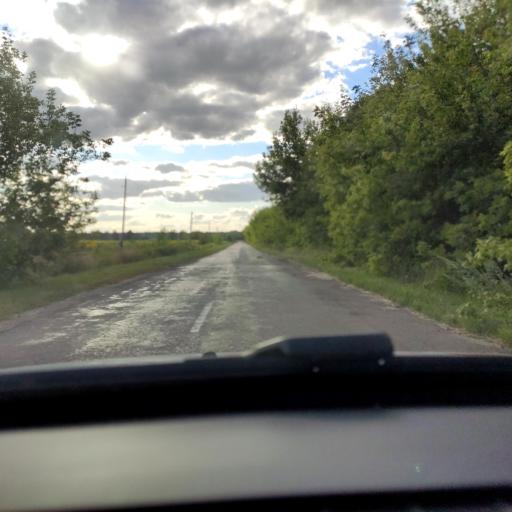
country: RU
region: Voronezj
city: Orlovo
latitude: 51.6427
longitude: 39.7423
